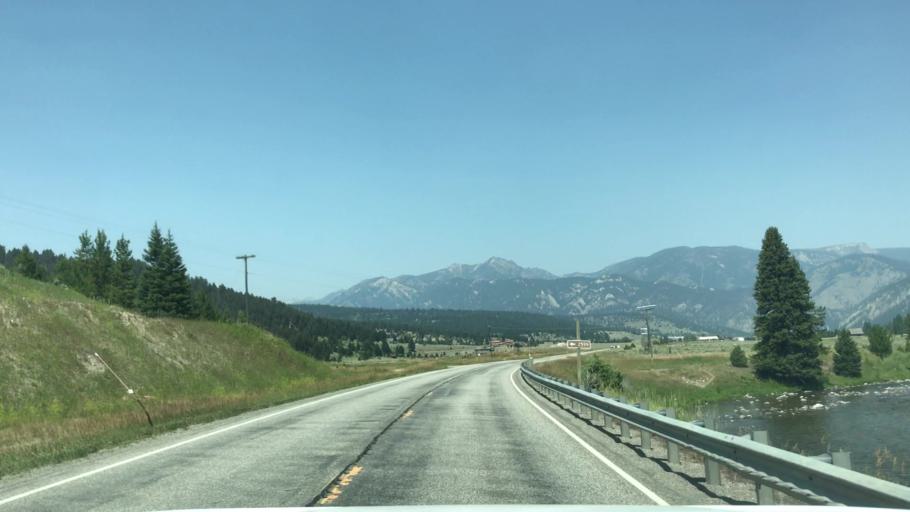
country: US
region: Montana
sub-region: Gallatin County
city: Big Sky
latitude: 45.2116
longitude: -111.2471
